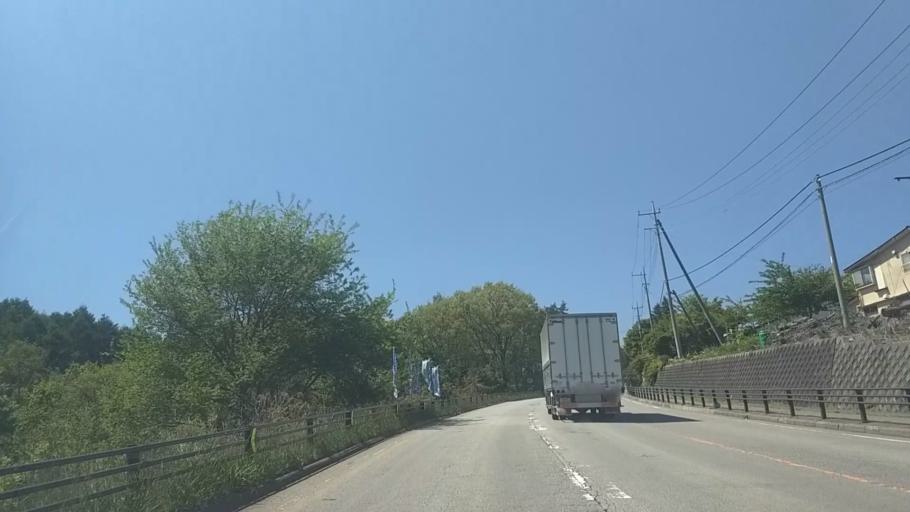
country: JP
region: Yamanashi
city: Nirasaki
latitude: 35.9108
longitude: 138.4438
